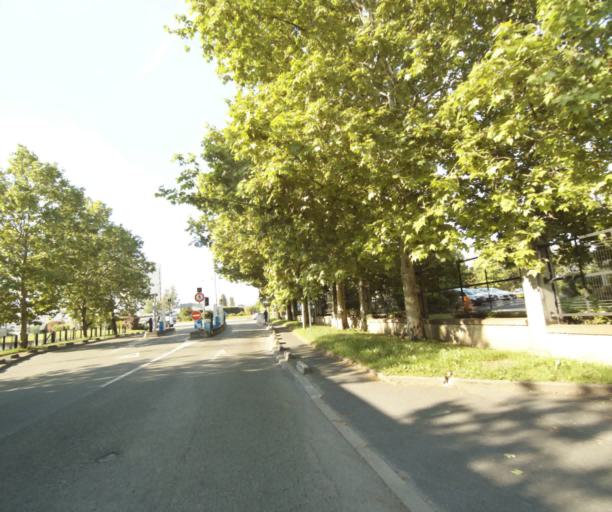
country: FR
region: Ile-de-France
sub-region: Departement des Hauts-de-Seine
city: Bois-Colombes
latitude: 48.9368
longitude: 2.2671
